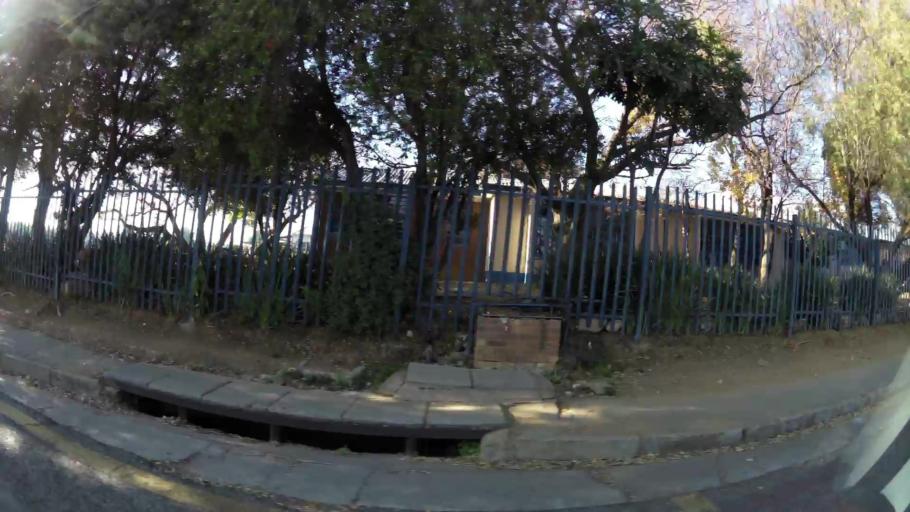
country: ZA
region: Gauteng
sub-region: City of Johannesburg Metropolitan Municipality
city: Modderfontein
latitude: -26.1342
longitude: 28.1562
